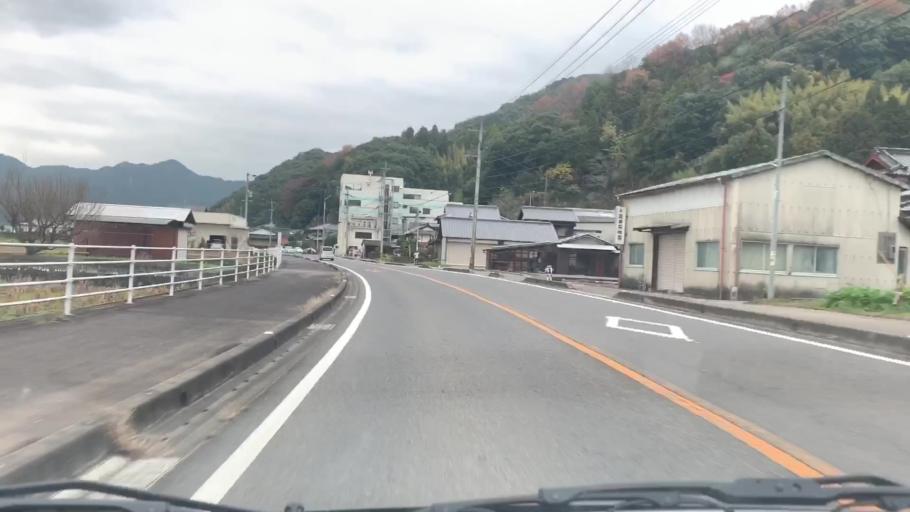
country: JP
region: Saga Prefecture
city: Kashima
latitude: 33.1285
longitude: 130.0532
